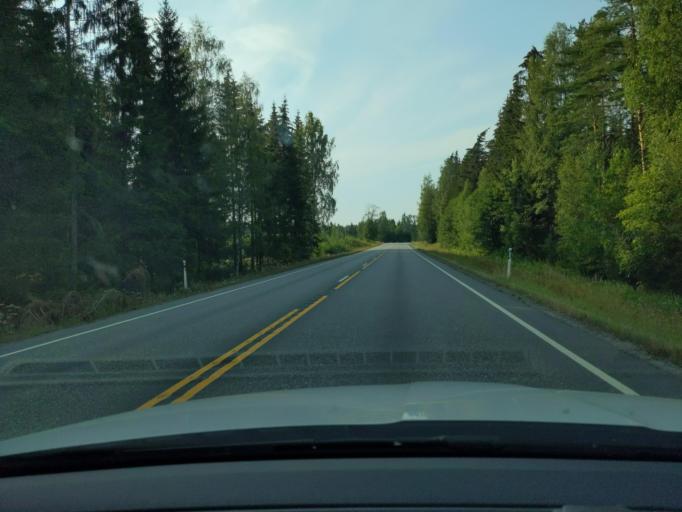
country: FI
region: Paijanne Tavastia
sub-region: Lahti
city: Padasjoki
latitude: 61.3191
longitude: 25.2844
